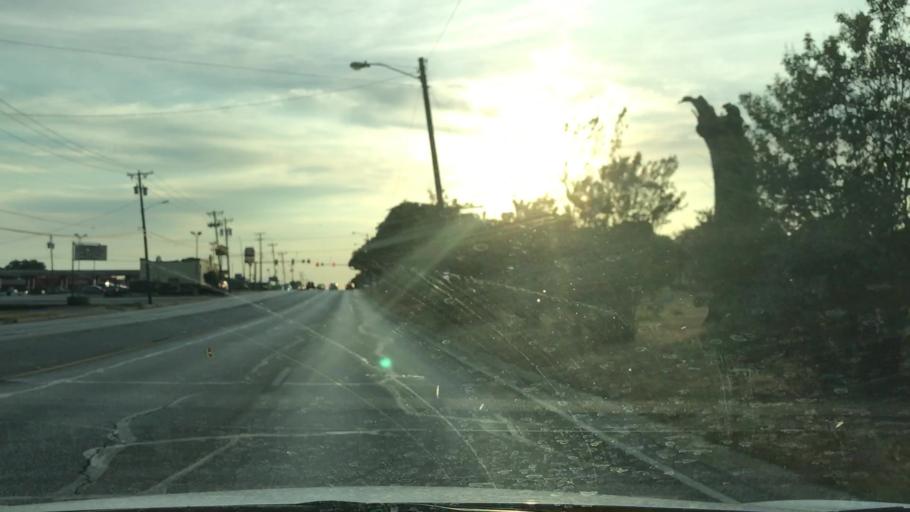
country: US
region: Texas
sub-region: Tarrant County
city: Haltom City
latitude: 32.7951
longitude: -97.2886
